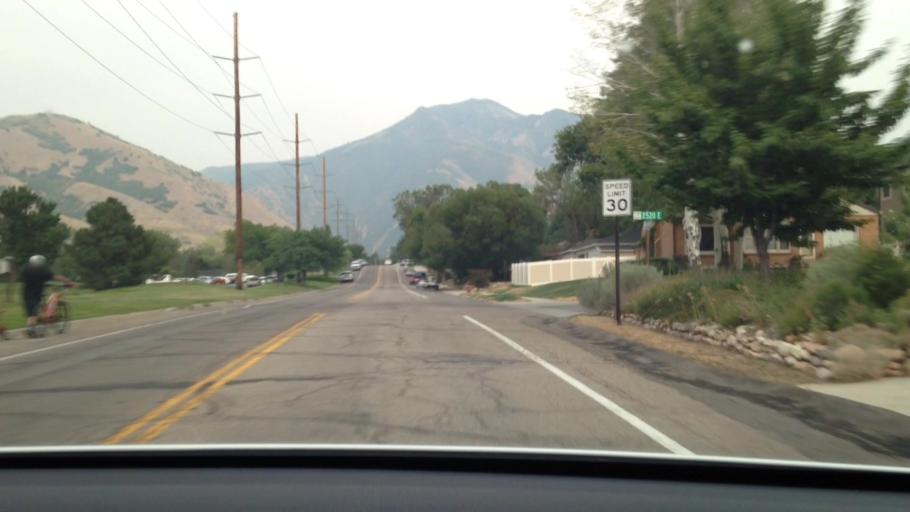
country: US
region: Utah
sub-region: Salt Lake County
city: Canyon Rim
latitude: 40.7113
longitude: -111.8196
